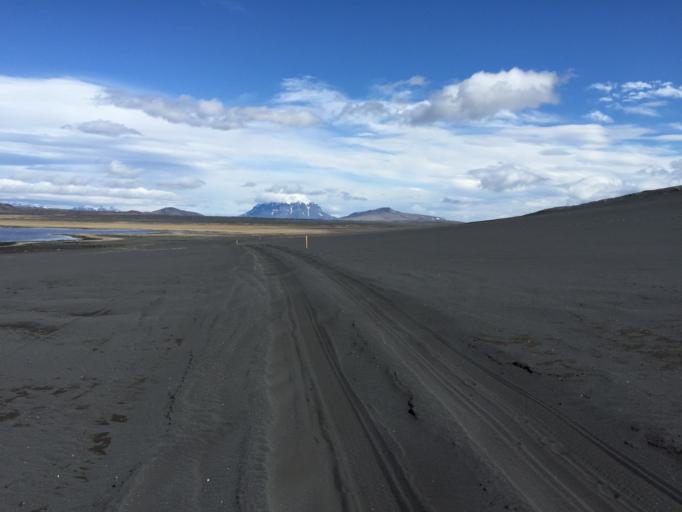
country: IS
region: Northeast
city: Laugar
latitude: 64.9875
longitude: -16.5482
